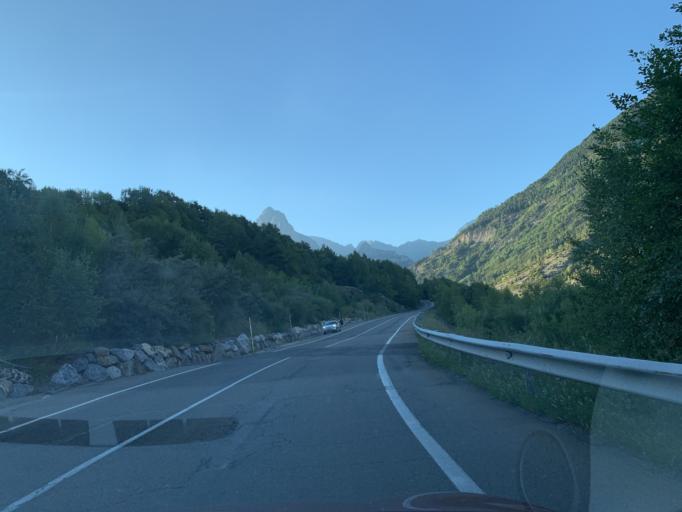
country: ES
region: Aragon
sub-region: Provincia de Huesca
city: Sallent de Gallego
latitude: 42.7543
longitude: -0.3198
